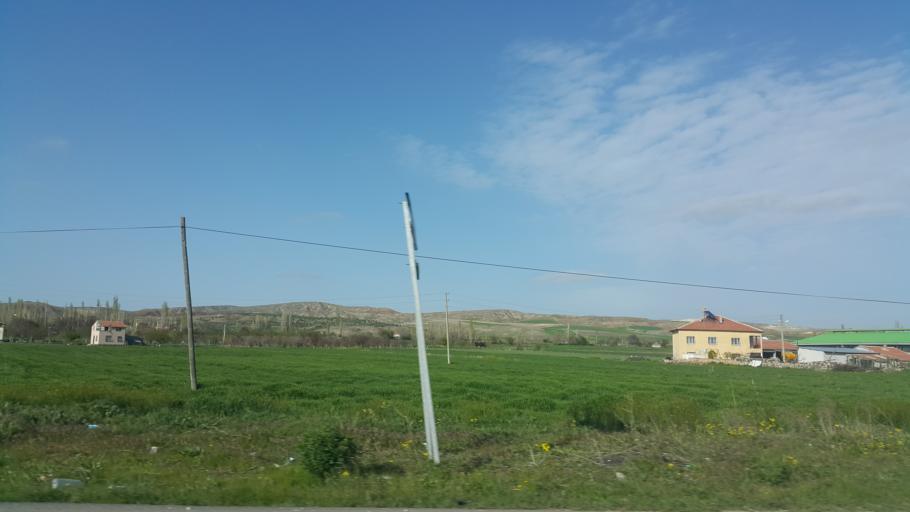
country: TR
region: Aksaray
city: Acipinar
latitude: 38.4853
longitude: 33.8852
